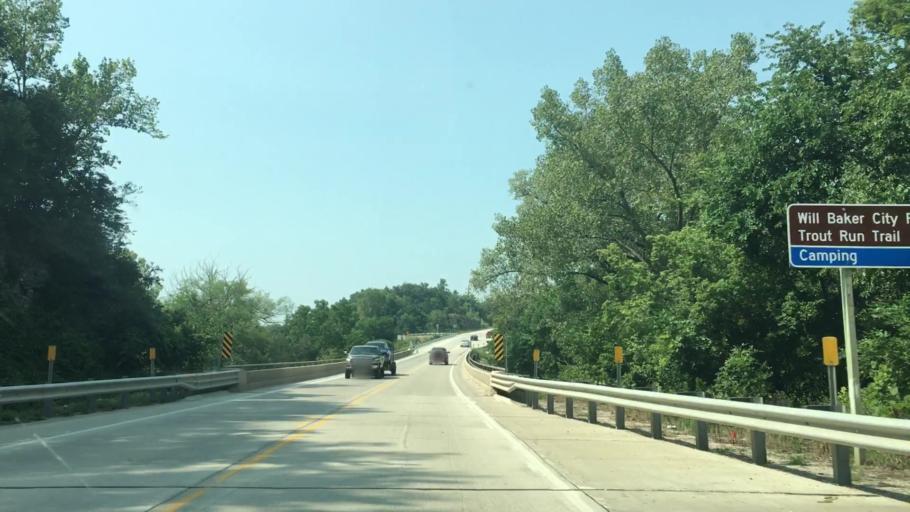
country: US
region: Iowa
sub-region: Winneshiek County
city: Decorah
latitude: 43.2981
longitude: -91.8112
